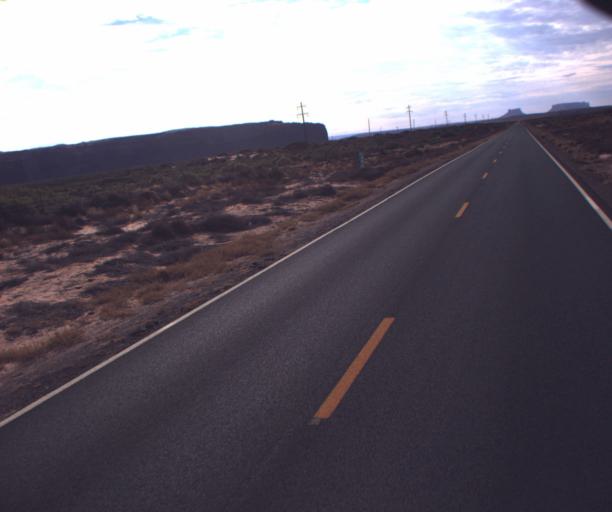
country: US
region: Arizona
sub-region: Apache County
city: Many Farms
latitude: 36.6498
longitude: -109.5918
